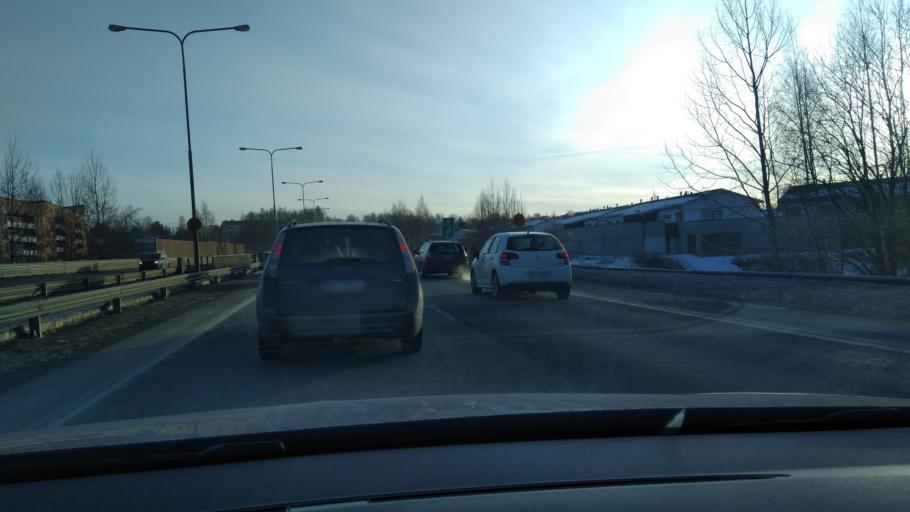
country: FI
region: Pirkanmaa
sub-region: Tampere
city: Pirkkala
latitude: 61.5046
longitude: 23.6816
